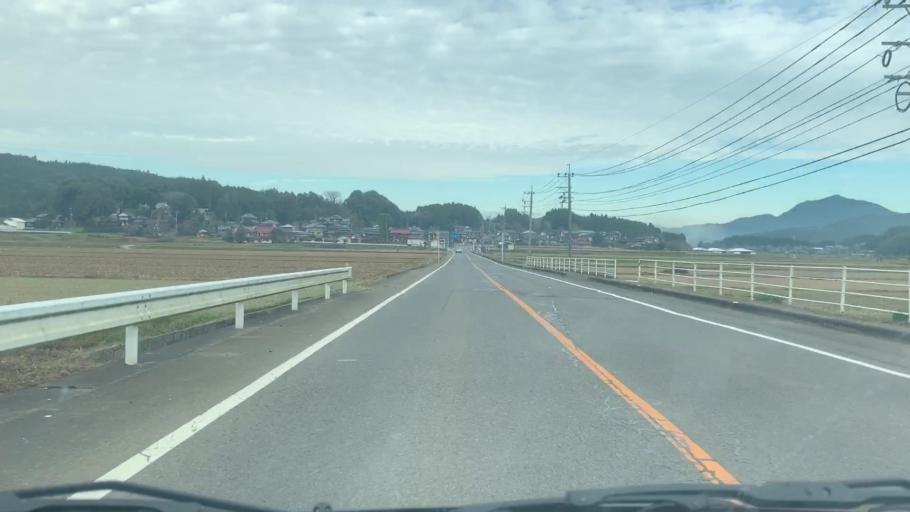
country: JP
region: Saga Prefecture
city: Takeocho-takeo
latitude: 33.2137
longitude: 129.9631
